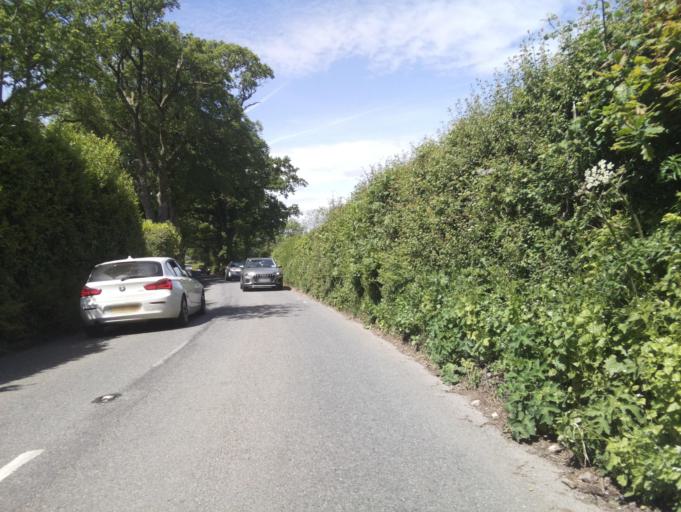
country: GB
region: England
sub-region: Devon
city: Ottery St Mary
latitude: 50.8206
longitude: -3.2697
